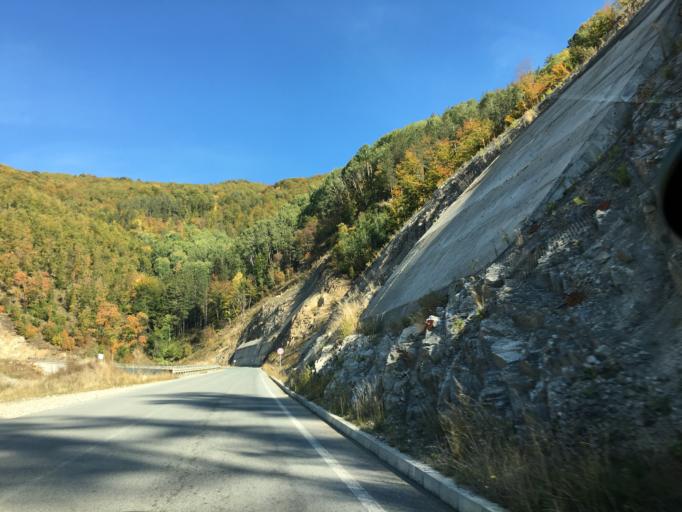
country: BG
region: Smolyan
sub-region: Obshtina Devin
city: Devin
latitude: 41.7679
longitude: 24.4499
